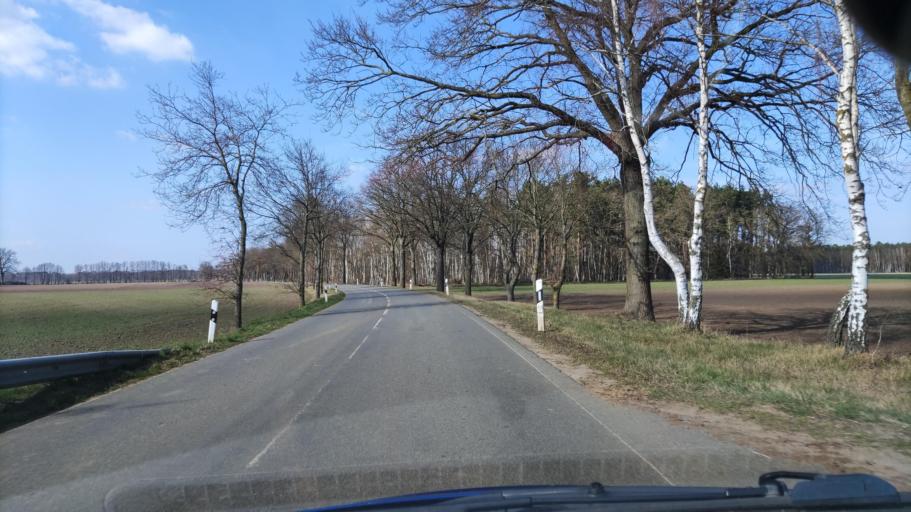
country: DE
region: Lower Saxony
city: Langendorf
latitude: 53.0642
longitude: 11.2316
